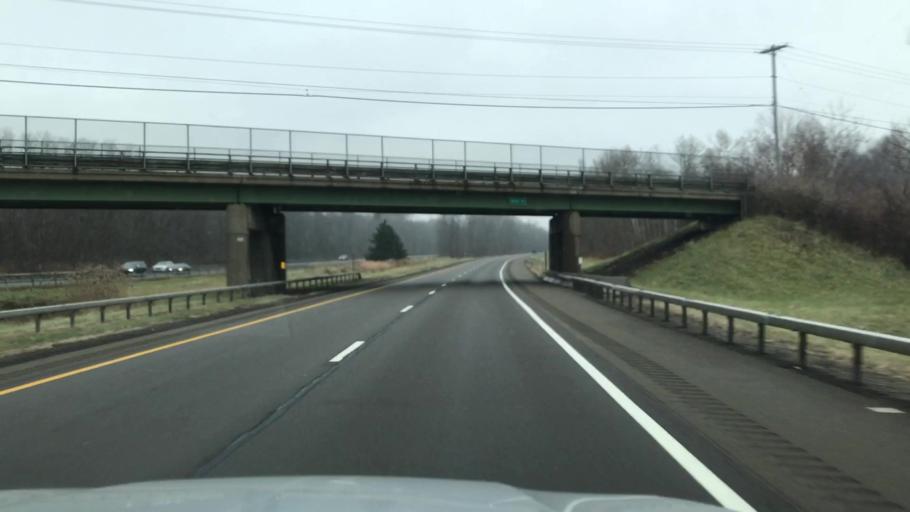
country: US
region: New York
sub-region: Chautauqua County
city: Fredonia
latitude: 42.4459
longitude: -79.3770
